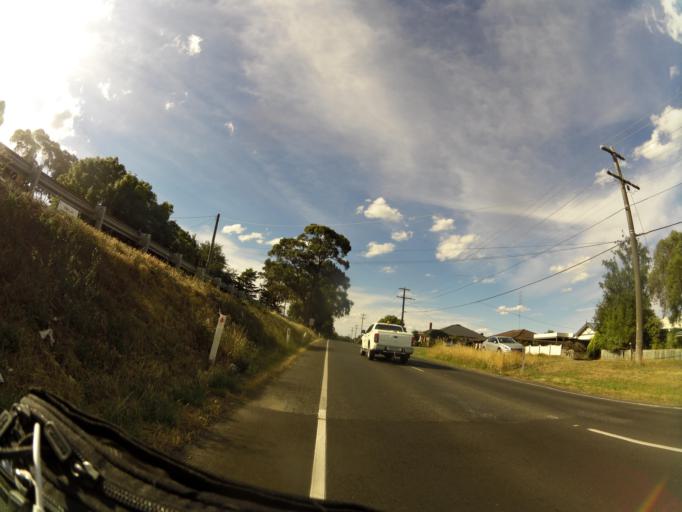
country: AU
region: Victoria
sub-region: Ballarat North
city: Mount Clear
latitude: -37.5996
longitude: 143.8681
